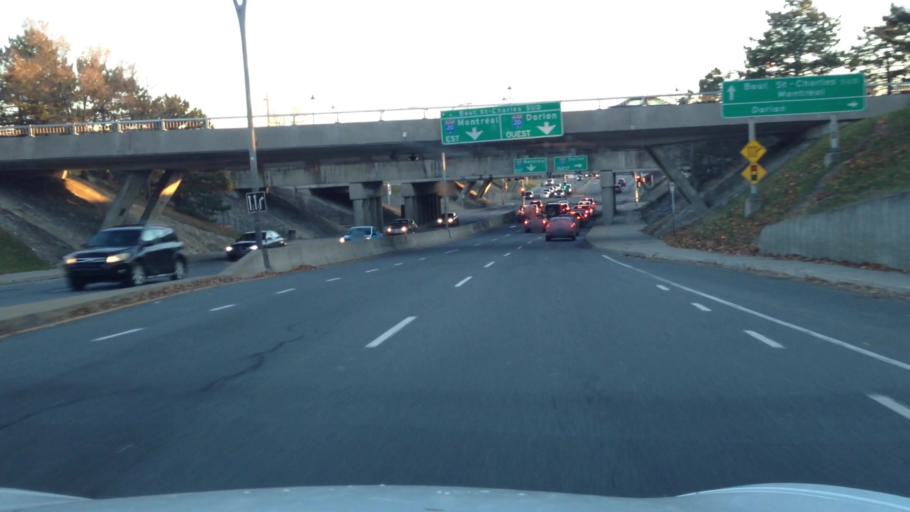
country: CA
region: Quebec
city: Beaconsfield
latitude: 45.4358
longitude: -73.8477
